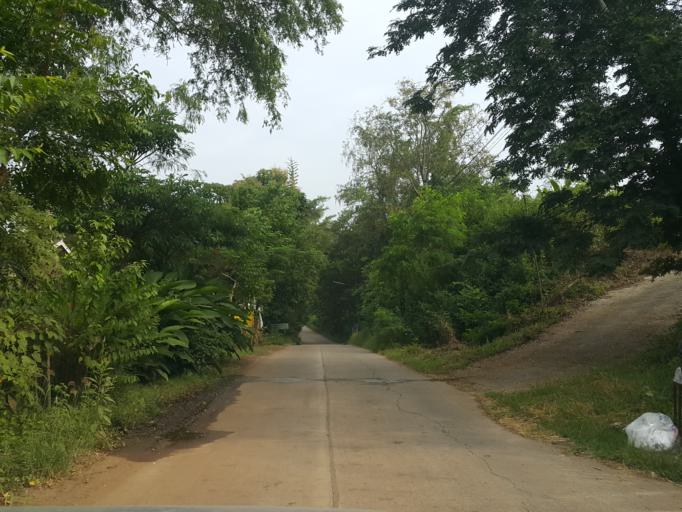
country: TH
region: Chiang Mai
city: Pai
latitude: 19.3666
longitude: 98.4499
